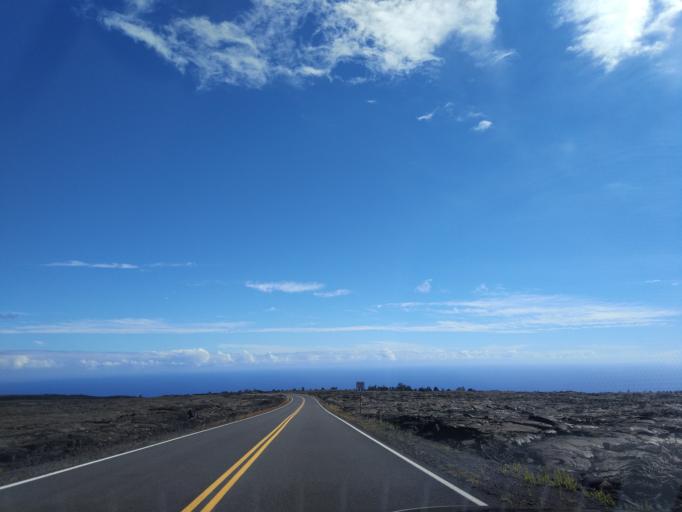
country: US
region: Hawaii
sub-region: Hawaii County
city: Volcano
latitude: 19.3351
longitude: -155.2024
